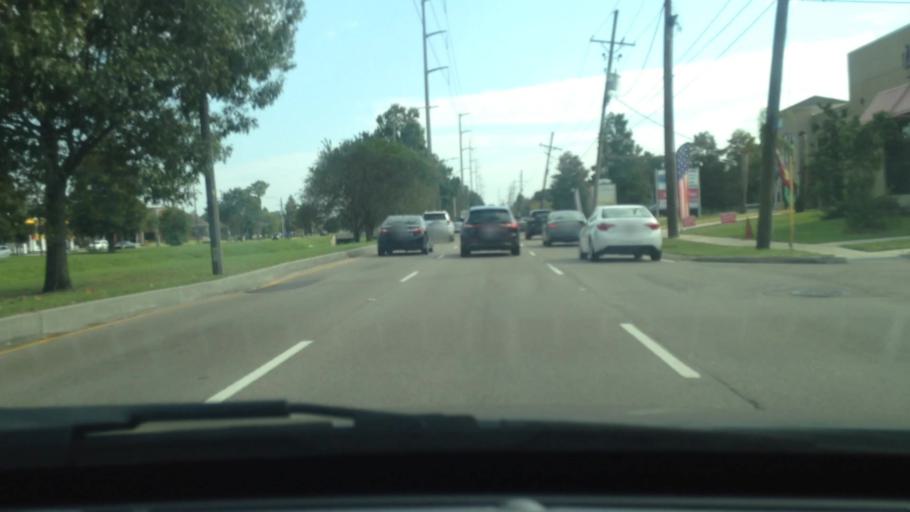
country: US
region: Louisiana
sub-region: Jefferson Parish
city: Terrytown
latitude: 29.9269
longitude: -90.0264
